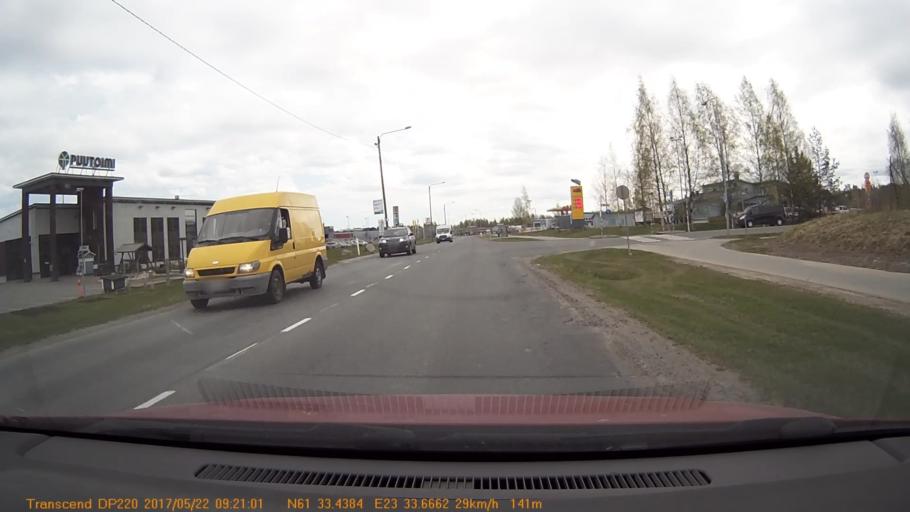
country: FI
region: Pirkanmaa
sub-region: Tampere
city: Yloejaervi
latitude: 61.5574
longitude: 23.5611
